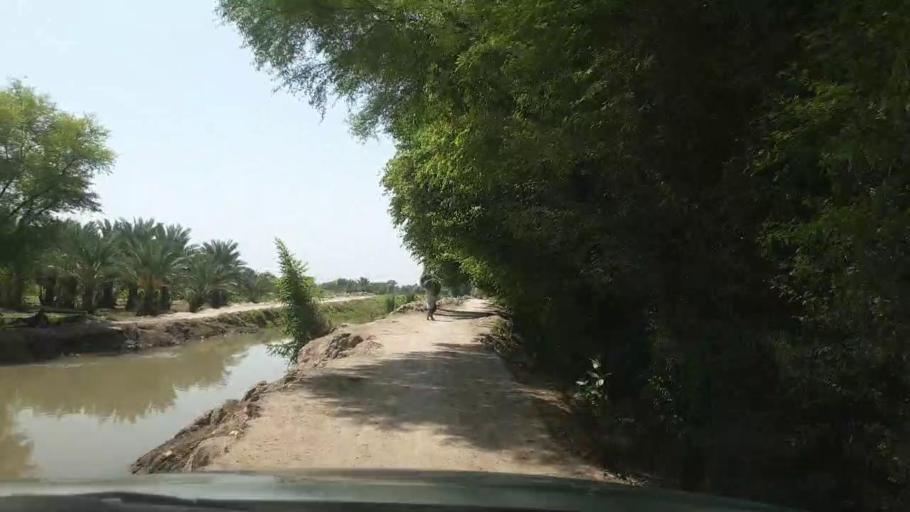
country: PK
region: Sindh
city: Rohri
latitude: 27.6533
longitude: 68.9832
